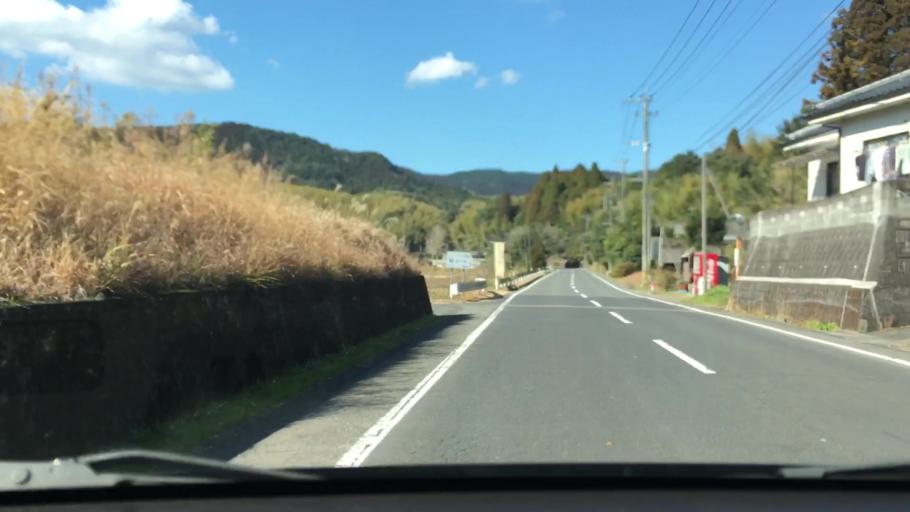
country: JP
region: Kagoshima
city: Ijuin
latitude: 31.7051
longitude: 130.4461
